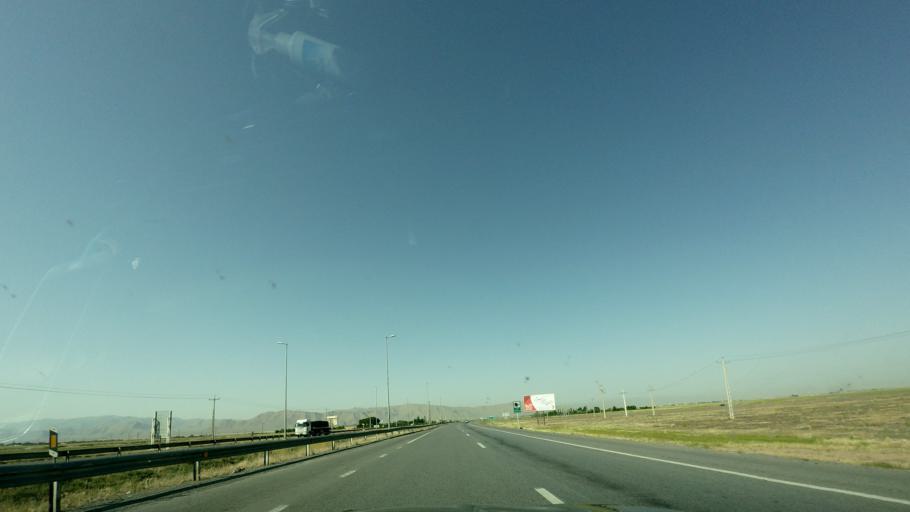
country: IR
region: Markazi
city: Ashtian
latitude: 34.1886
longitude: 50.0528
